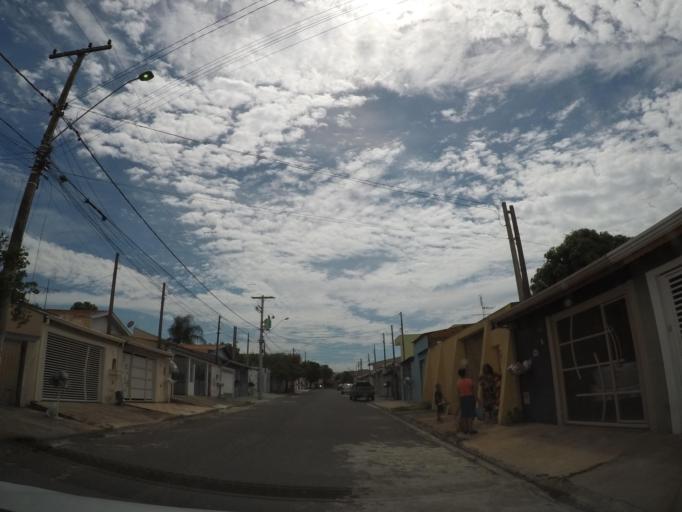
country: BR
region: Sao Paulo
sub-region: Hortolandia
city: Hortolandia
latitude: -22.8364
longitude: -47.1846
